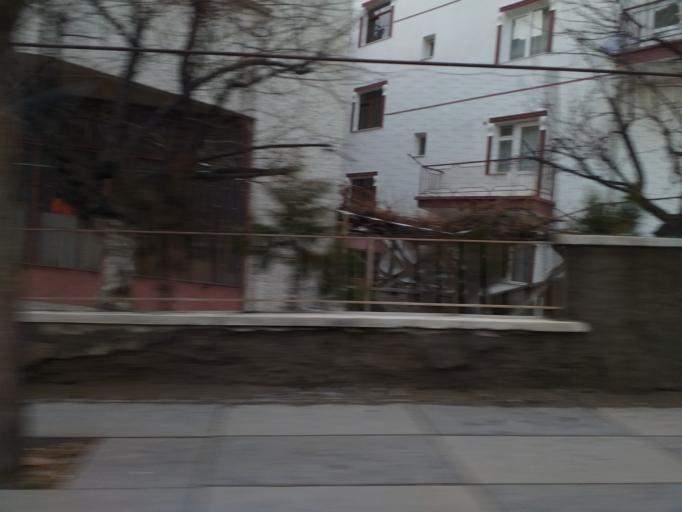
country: TR
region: Ankara
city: Ankara
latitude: 39.9764
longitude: 32.8187
